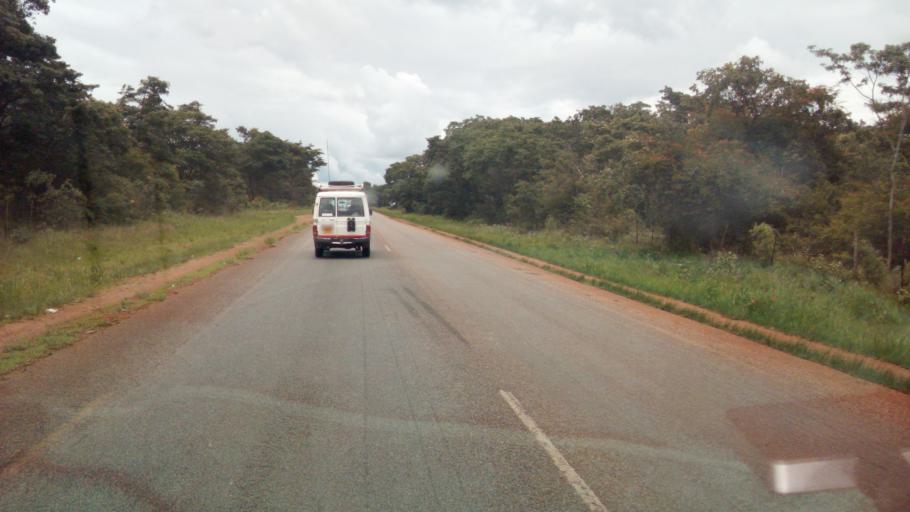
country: ZW
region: Harare
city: Harare
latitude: -17.7092
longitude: 31.0128
